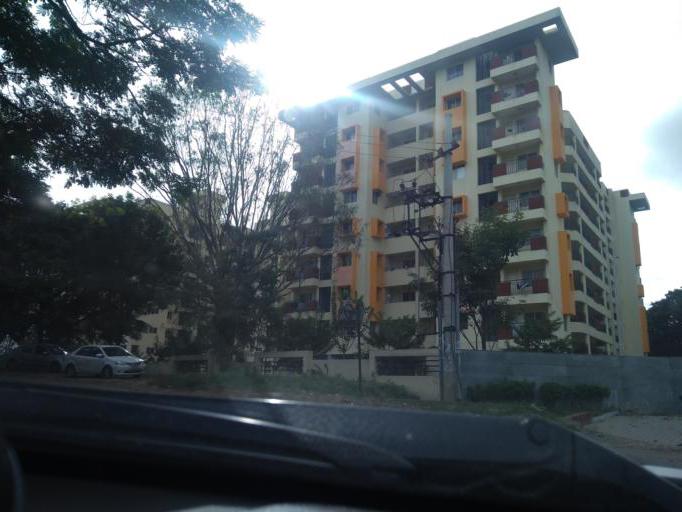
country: IN
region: Karnataka
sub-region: Bangalore Urban
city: Bangalore
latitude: 12.9920
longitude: 77.6514
